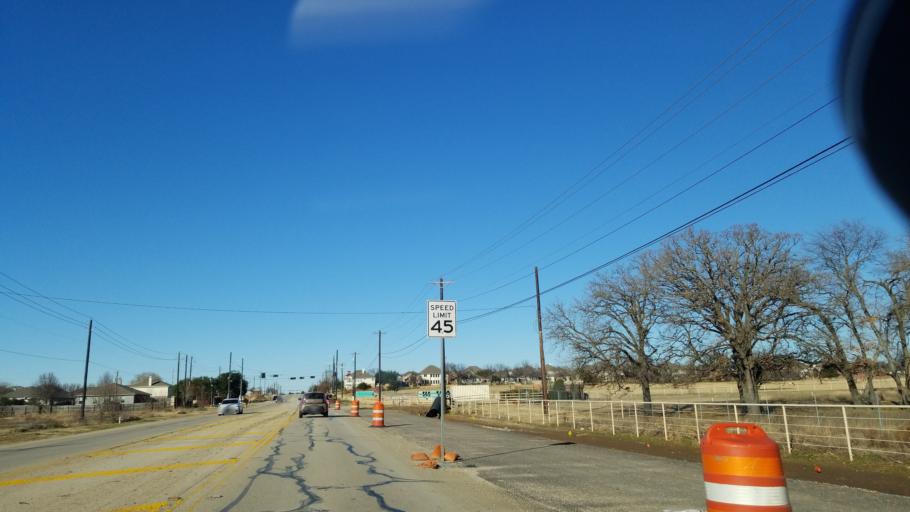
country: US
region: Texas
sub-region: Denton County
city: Corinth
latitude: 33.1400
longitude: -97.1052
